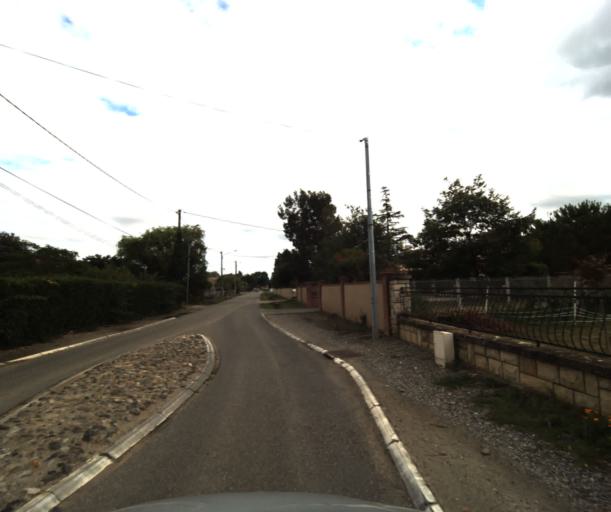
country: FR
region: Midi-Pyrenees
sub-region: Departement de la Haute-Garonne
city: Eaunes
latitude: 43.4293
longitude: 1.3472
